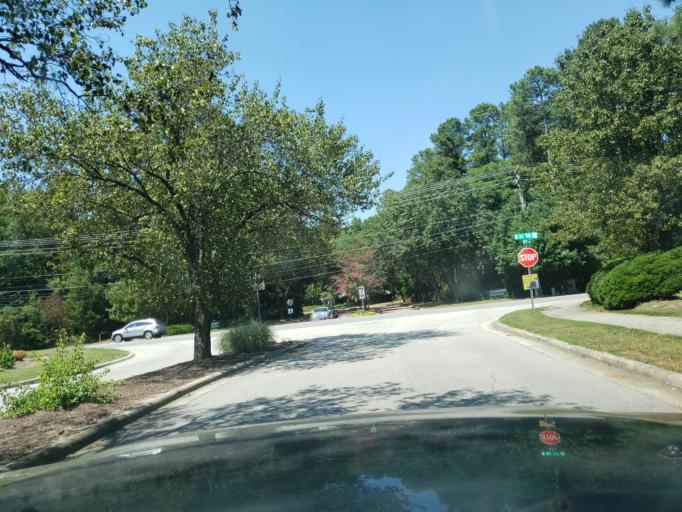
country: US
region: North Carolina
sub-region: Durham County
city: Durham
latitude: 35.9118
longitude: -78.9458
